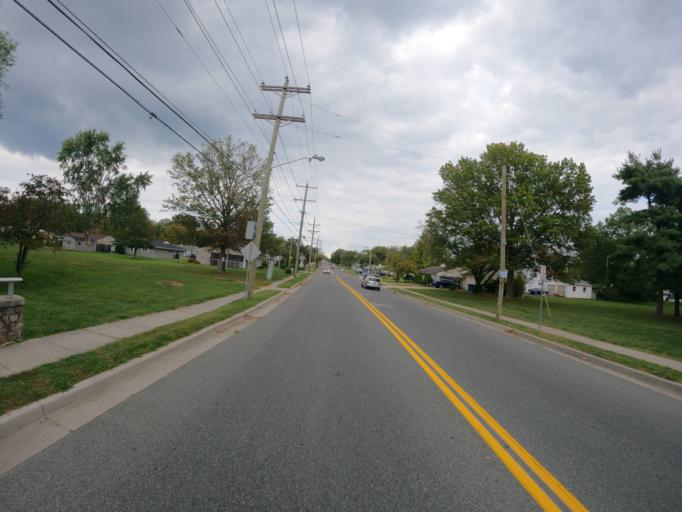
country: US
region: Delaware
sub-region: New Castle County
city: Brookside
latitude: 39.6702
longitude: -75.7276
